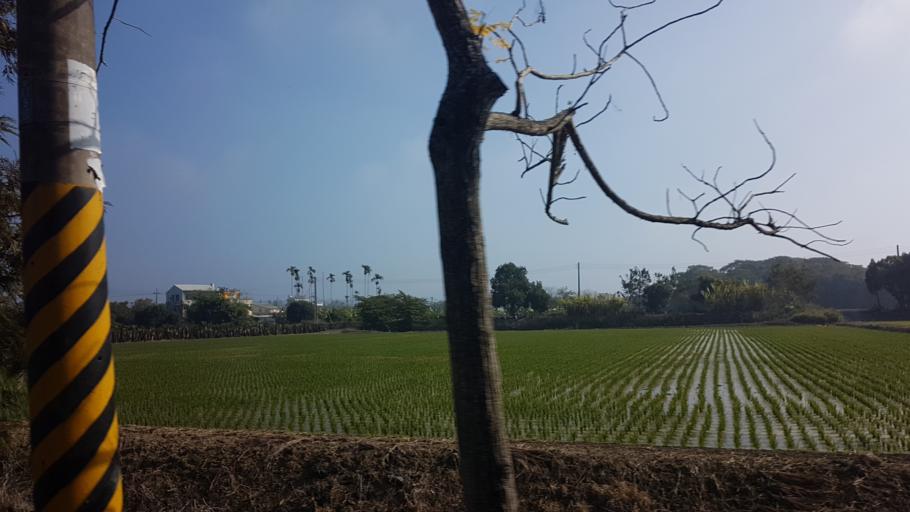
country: TW
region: Taiwan
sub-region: Chiayi
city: Jiayi Shi
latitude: 23.3777
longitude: 120.4525
